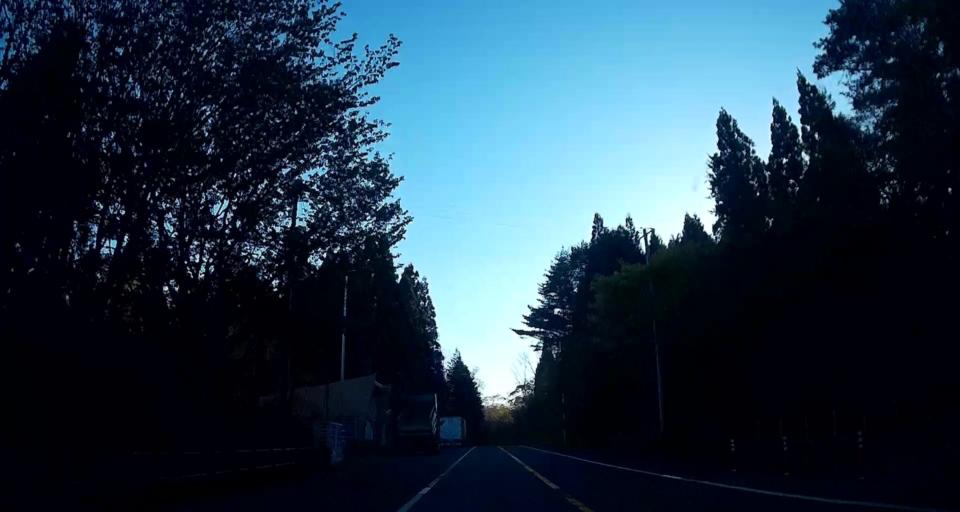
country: JP
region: Iwate
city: Miyako
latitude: 39.6545
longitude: 141.9642
